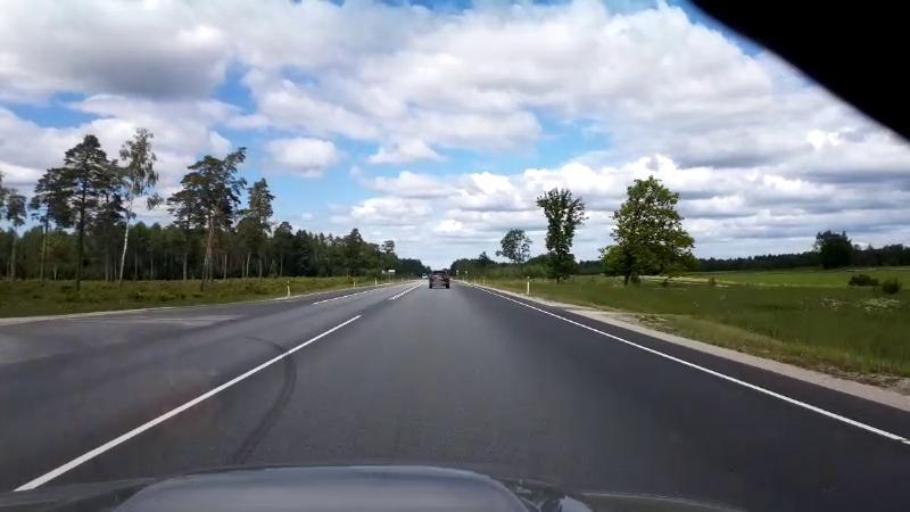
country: EE
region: Harju
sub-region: Nissi vald
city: Riisipere
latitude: 59.0634
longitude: 24.4494
